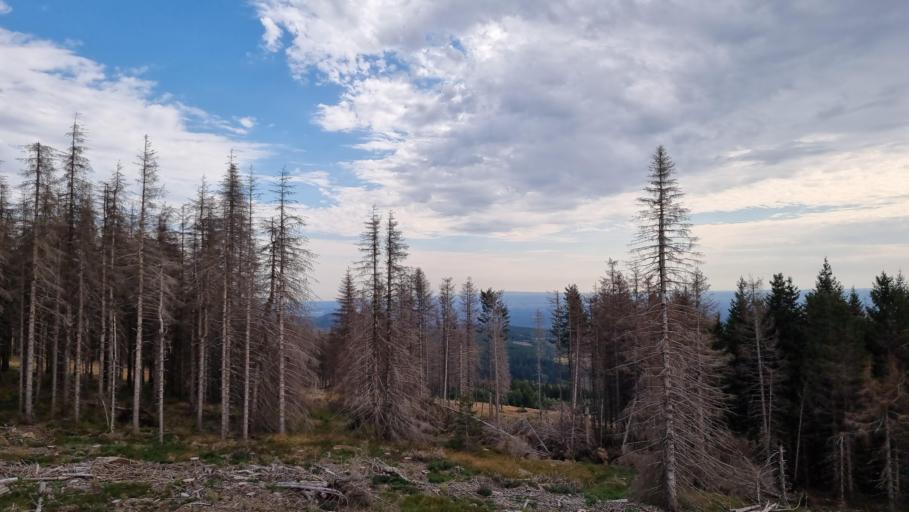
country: DE
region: Lower Saxony
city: Braunlage
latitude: 51.7517
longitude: 10.6172
